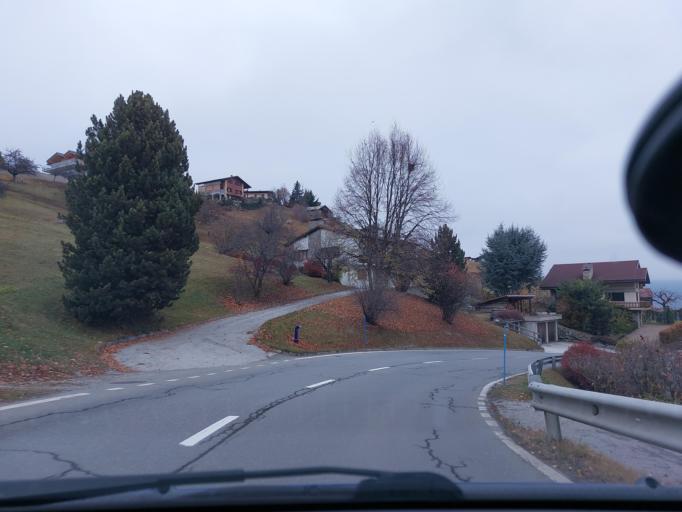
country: CH
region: Valais
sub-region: Conthey District
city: Basse-Nendaz
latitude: 46.1871
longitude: 7.3070
